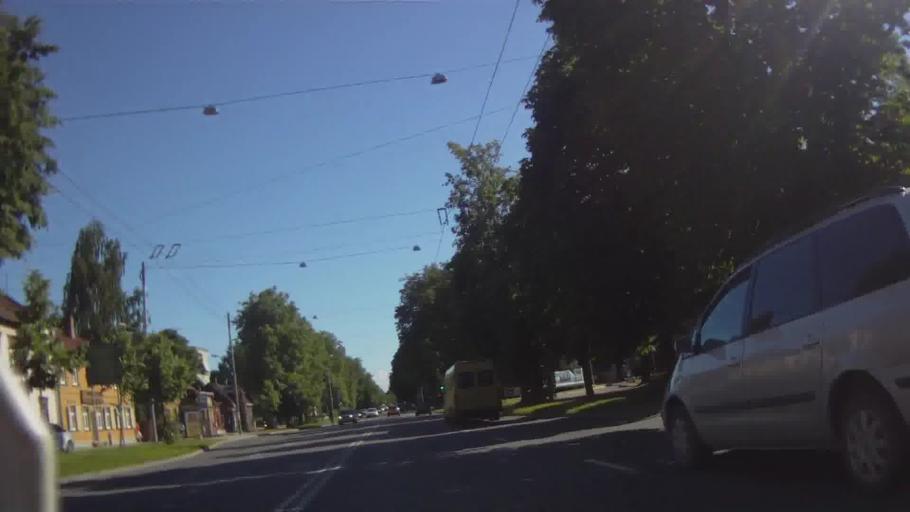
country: LV
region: Riga
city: Riga
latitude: 56.9173
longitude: 24.0880
